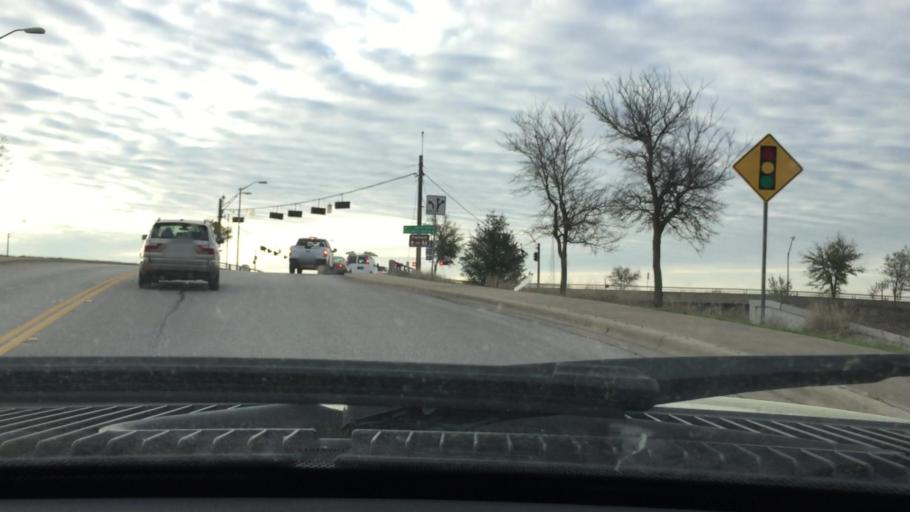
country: US
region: Texas
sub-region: Williamson County
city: Cedar Park
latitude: 30.5043
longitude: -97.8126
